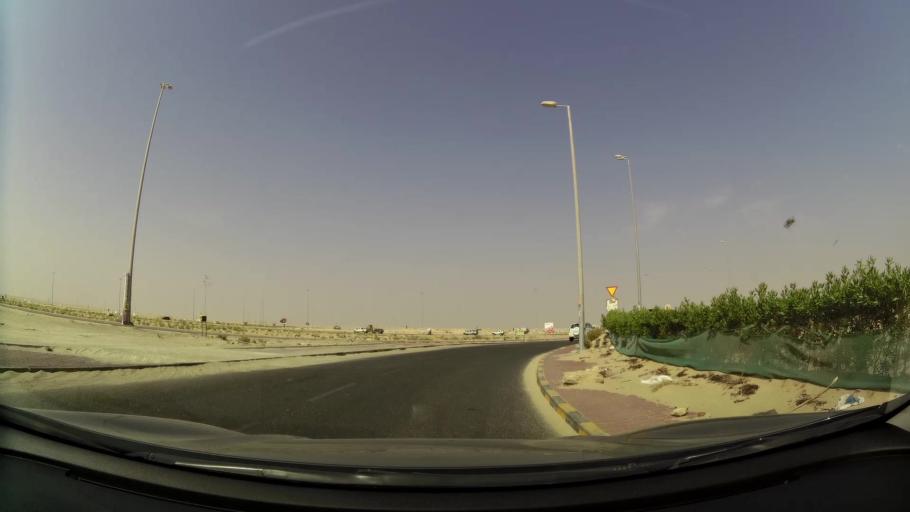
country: KW
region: Al Ahmadi
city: Al Wafrah
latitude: 28.8040
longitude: 48.0455
